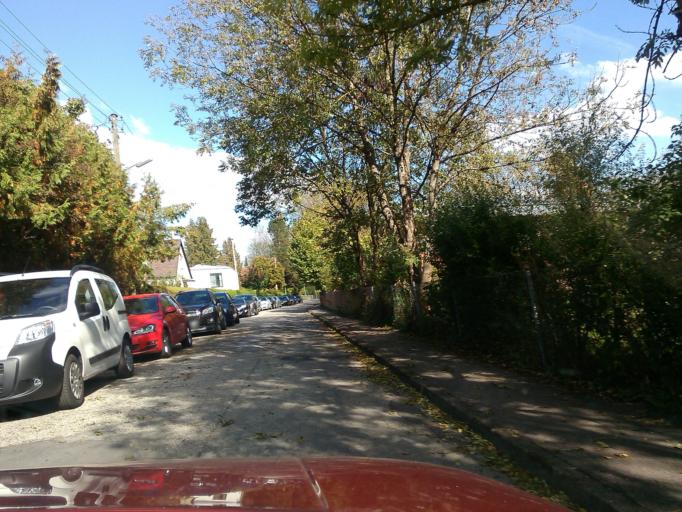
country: DE
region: Bavaria
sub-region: Upper Bavaria
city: Krailling
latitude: 48.0897
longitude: 11.4081
